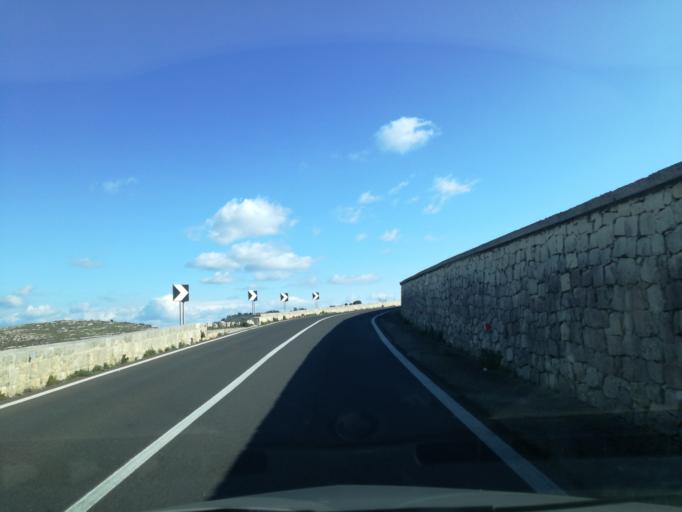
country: IT
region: Sicily
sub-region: Ragusa
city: Comiso
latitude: 36.9414
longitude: 14.6360
